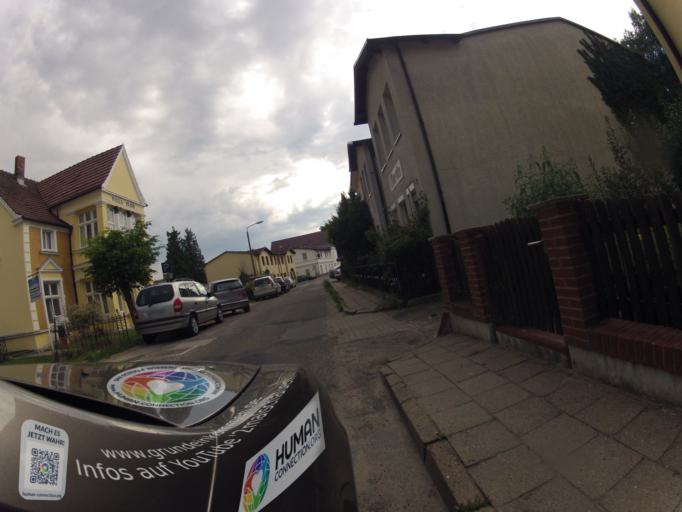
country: DE
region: Mecklenburg-Vorpommern
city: Seebad Heringsdorf
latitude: 53.9390
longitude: 14.1895
